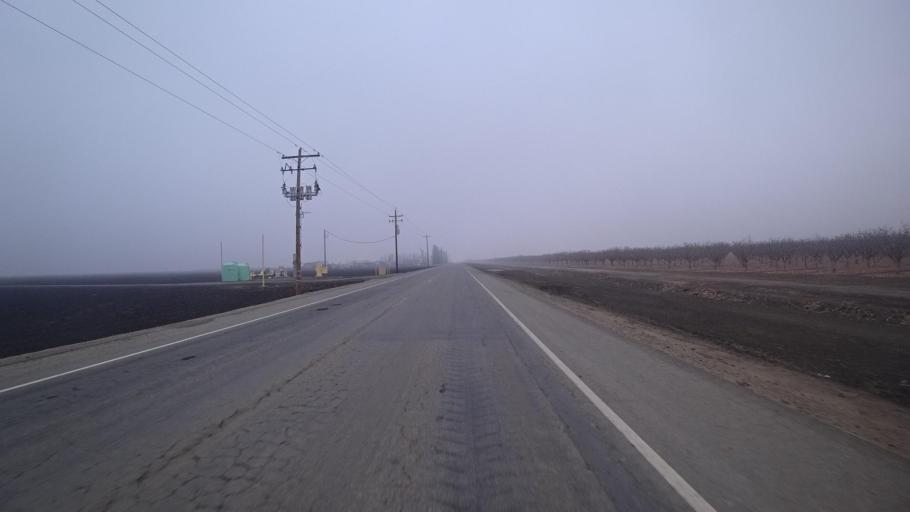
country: US
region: California
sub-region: Kern County
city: Buttonwillow
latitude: 35.4171
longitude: -119.5185
